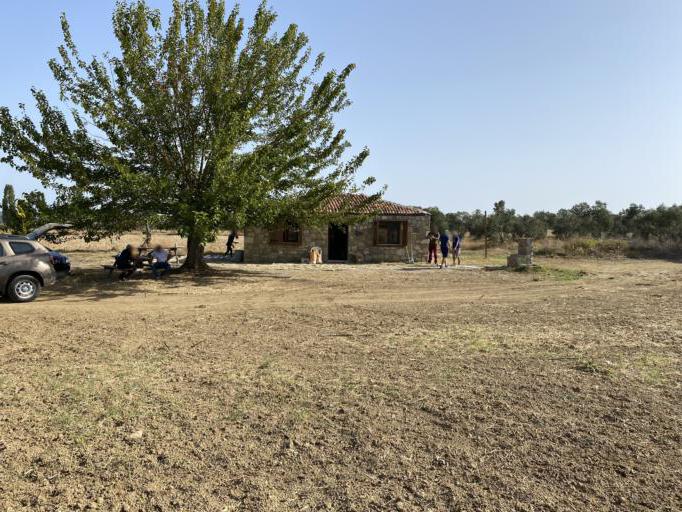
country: TR
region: Canakkale
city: Eceabat
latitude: 40.1823
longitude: 26.2864
